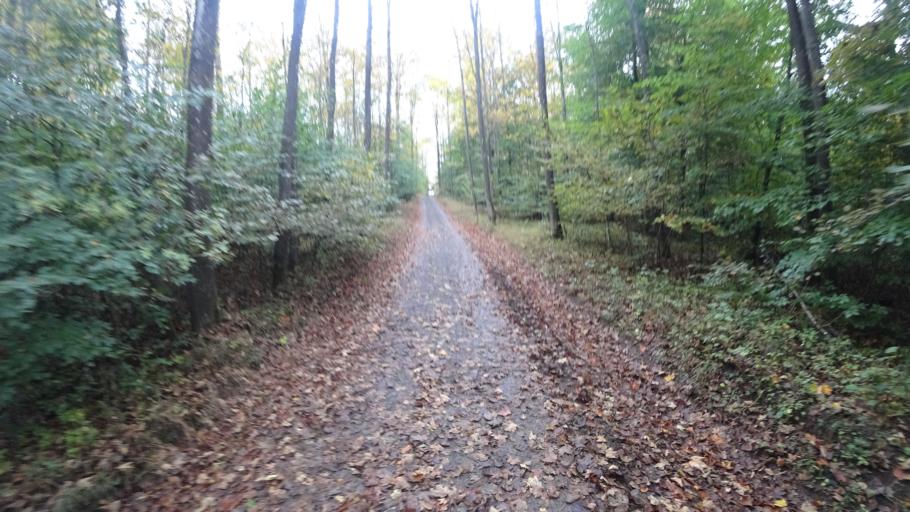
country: DE
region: Rheinland-Pfalz
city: Ruckeroth
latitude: 50.5596
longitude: 7.7663
